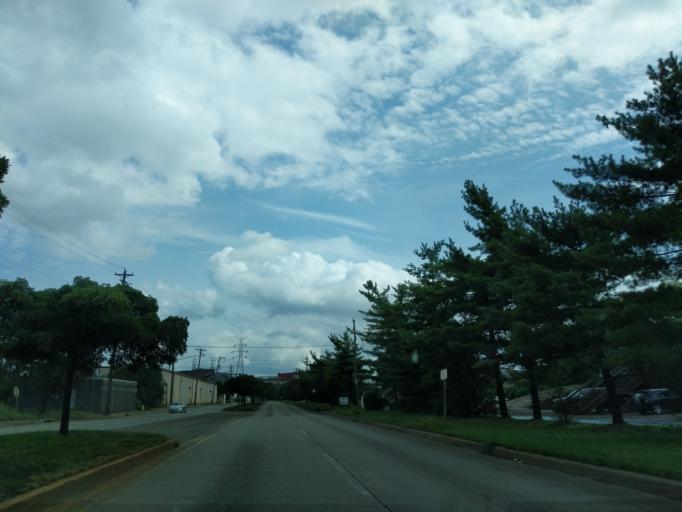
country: US
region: Kentucky
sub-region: Kenton County
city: Ludlow
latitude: 39.0968
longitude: -84.5307
